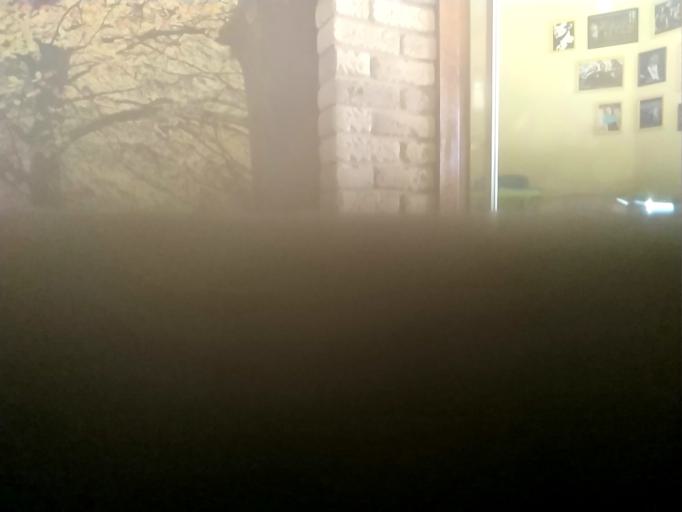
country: RU
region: Kaluga
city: Yukhnov
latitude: 54.8091
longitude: 35.0102
